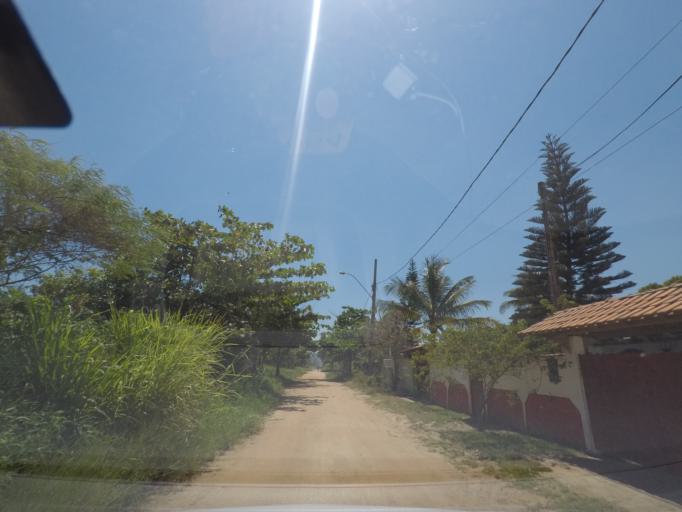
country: BR
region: Rio de Janeiro
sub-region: Marica
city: Marica
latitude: -22.9705
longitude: -42.9437
